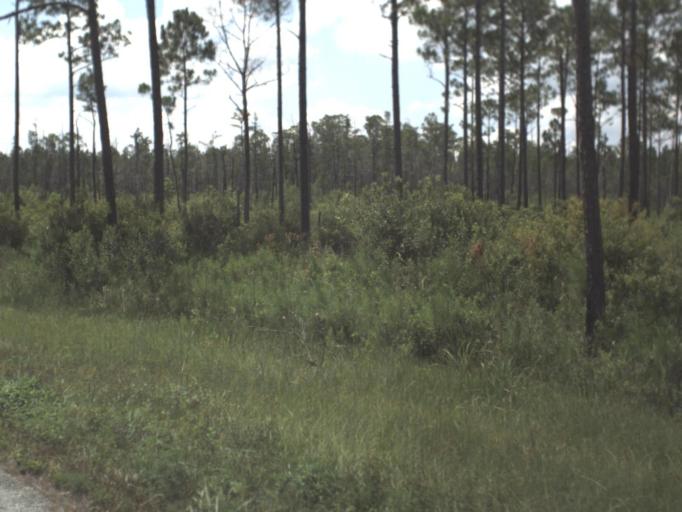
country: US
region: Florida
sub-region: Baker County
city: Macclenny
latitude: 30.5662
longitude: -82.4009
